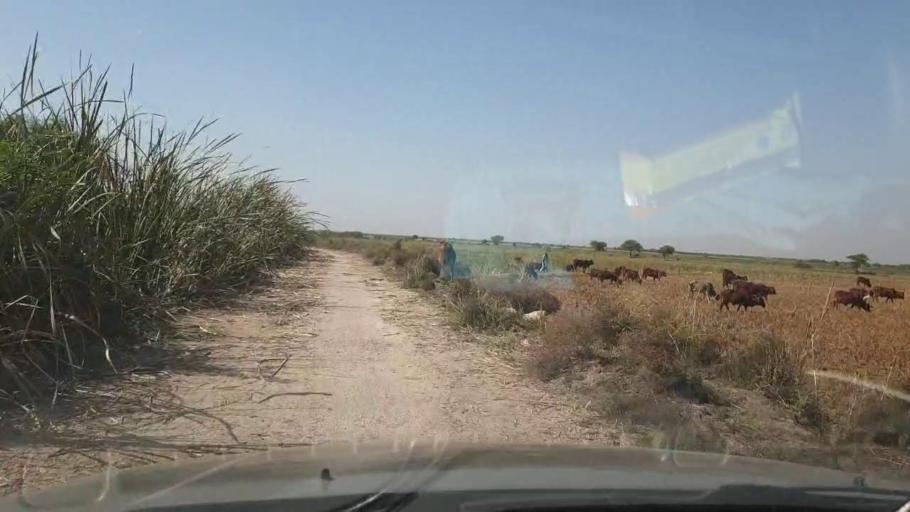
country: PK
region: Sindh
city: Daro Mehar
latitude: 24.9741
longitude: 68.1106
